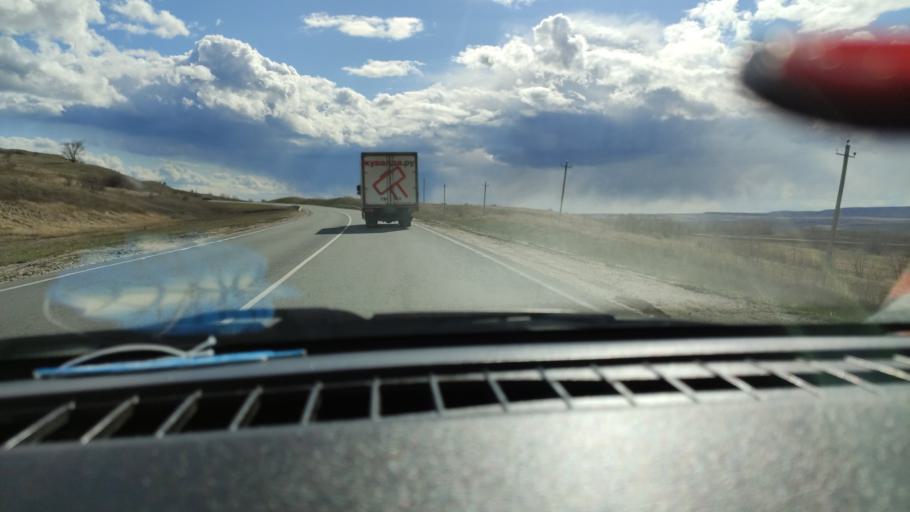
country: RU
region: Saratov
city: Alekseyevka
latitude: 52.3283
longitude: 47.9205
